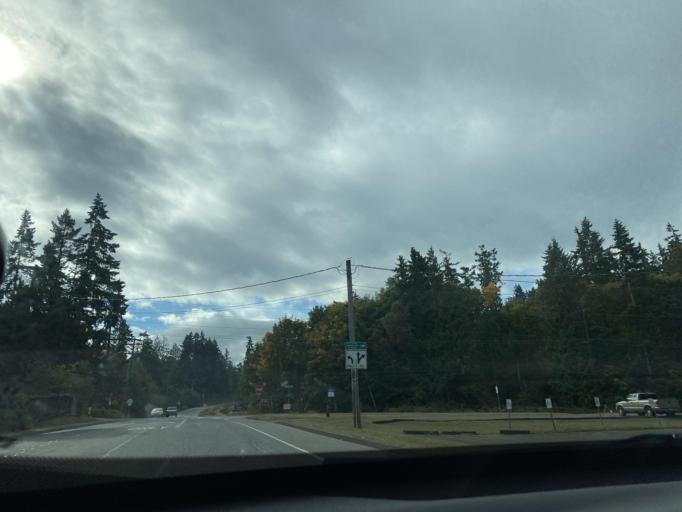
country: US
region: Washington
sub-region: Clallam County
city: Port Angeles
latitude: 48.1026
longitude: -123.4259
